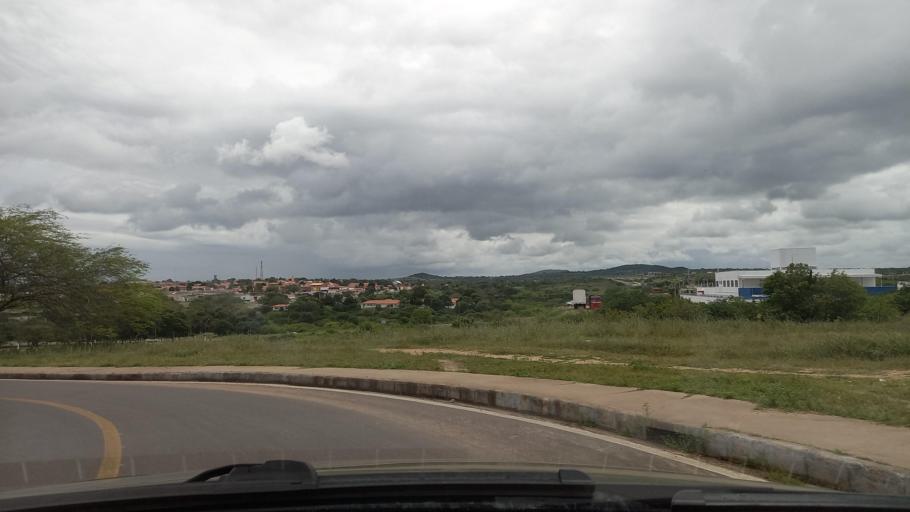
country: BR
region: Sergipe
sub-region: Caninde De Sao Francisco
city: Caninde de Sao Francisco
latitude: -9.6077
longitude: -37.7637
